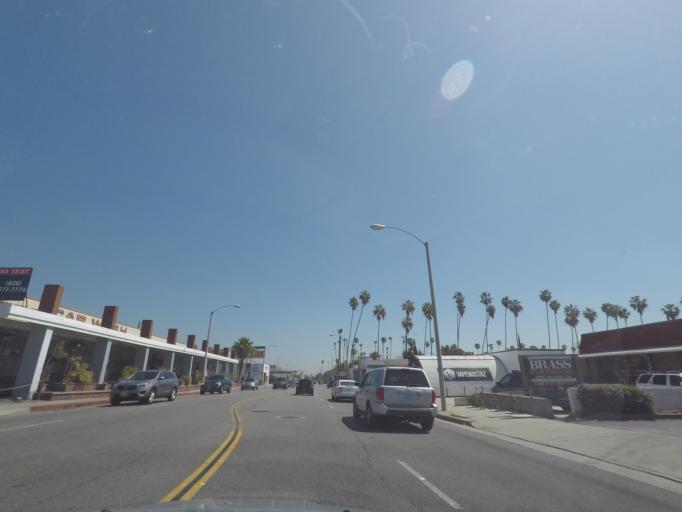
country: US
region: California
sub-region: Los Angeles County
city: Pasadena
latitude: 34.1495
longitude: -118.1210
